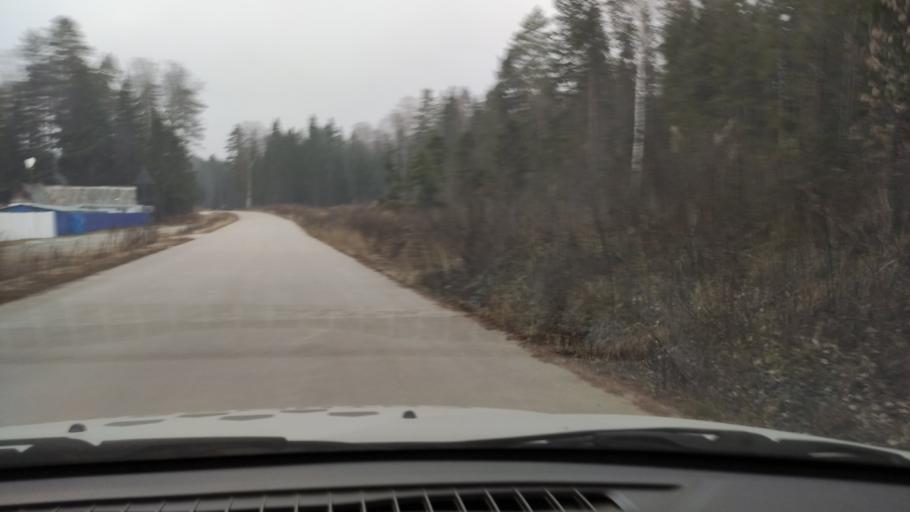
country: RU
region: Perm
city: Kondratovo
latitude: 58.0474
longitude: 56.1447
